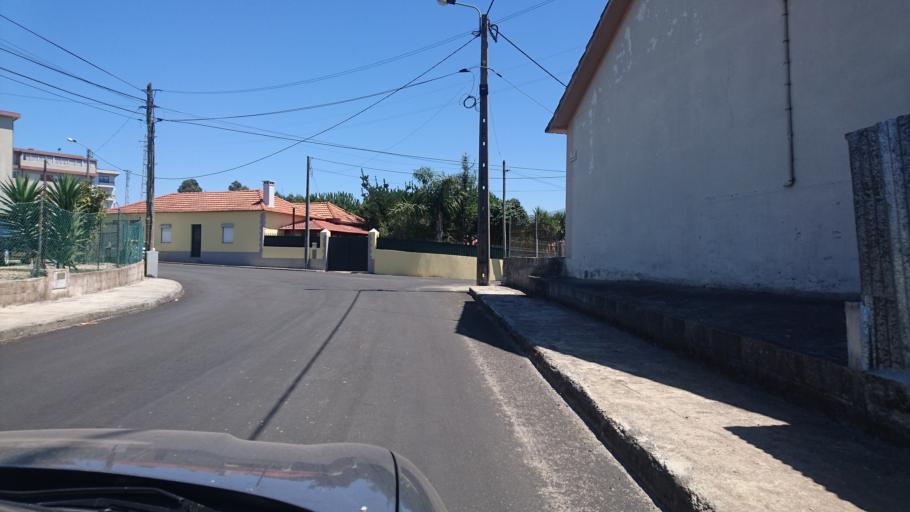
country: PT
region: Aveiro
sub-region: Espinho
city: Souto
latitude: 40.9835
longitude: -8.6057
